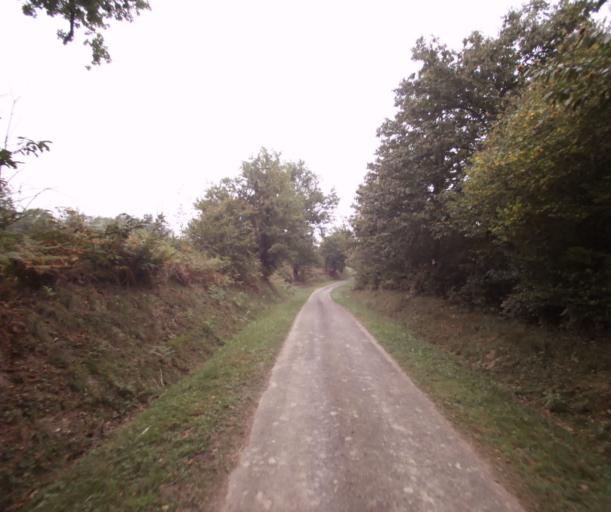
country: FR
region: Midi-Pyrenees
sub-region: Departement du Gers
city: Cazaubon
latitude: 43.9215
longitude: -0.1814
